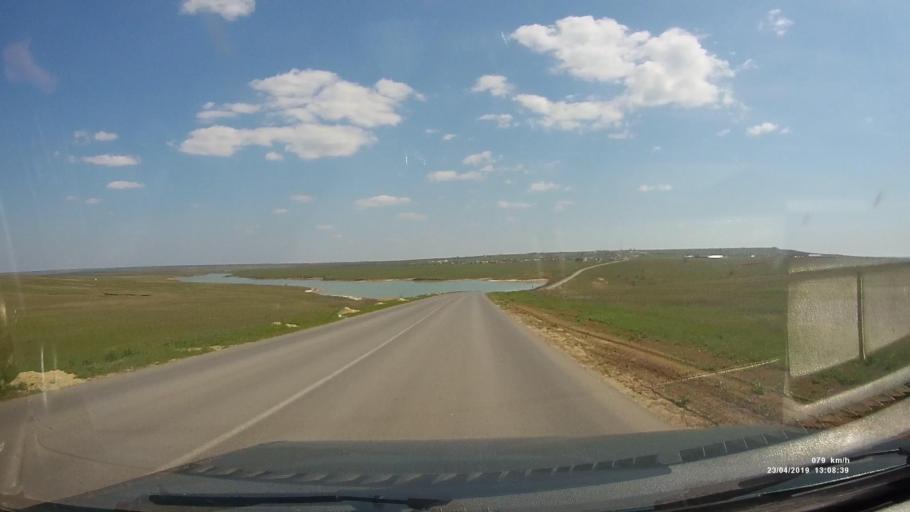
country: RU
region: Kalmykiya
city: Yashalta
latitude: 46.5811
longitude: 42.7781
